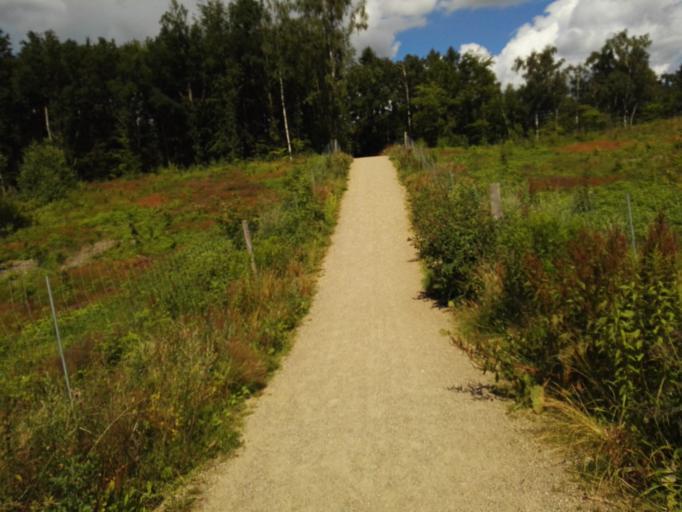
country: DK
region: Capital Region
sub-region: Ballerup Kommune
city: Ballerup
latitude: 55.7484
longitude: 12.3620
